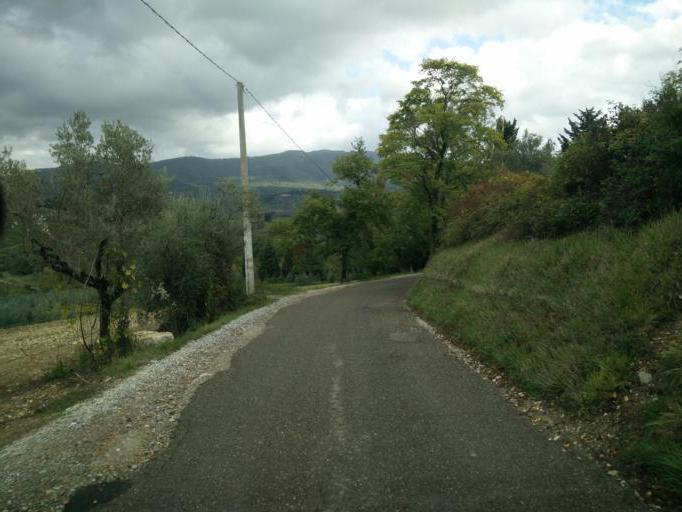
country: IT
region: Tuscany
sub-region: Province of Florence
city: Greve in Chianti
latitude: 43.5796
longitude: 11.2988
